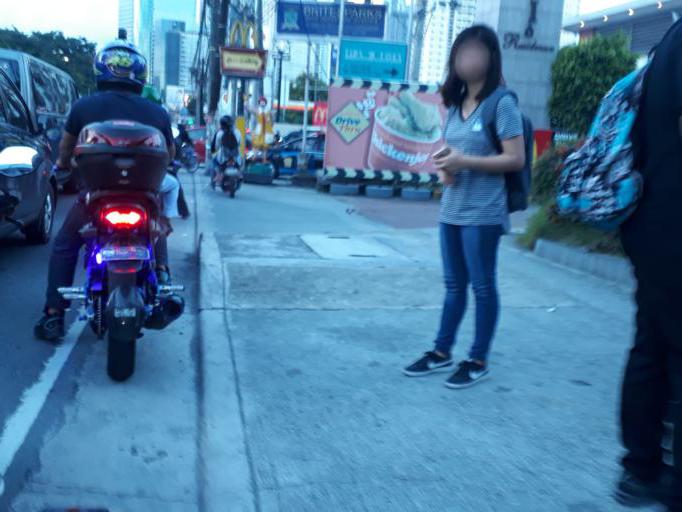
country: PH
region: Metro Manila
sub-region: Pasig
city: Pasig City
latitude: 14.6016
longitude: 121.0795
